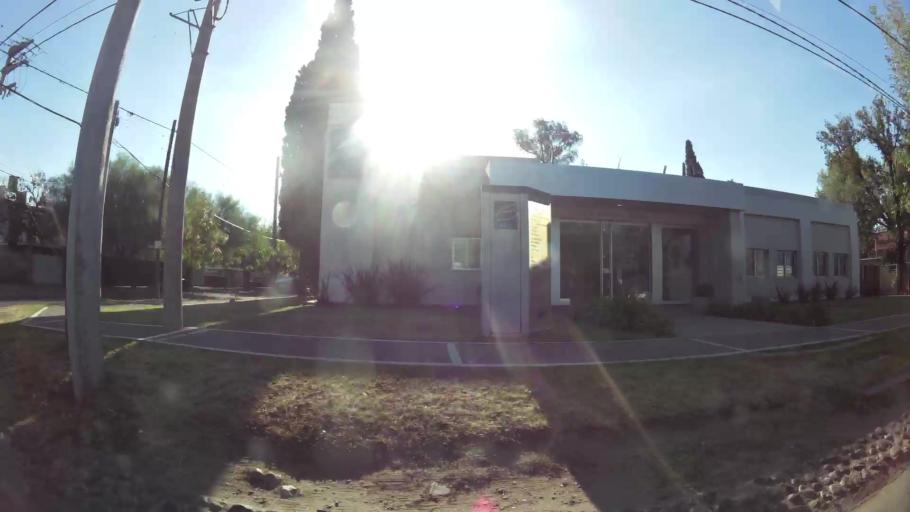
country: AR
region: Cordoba
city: Villa Allende
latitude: -31.3588
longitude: -64.2472
